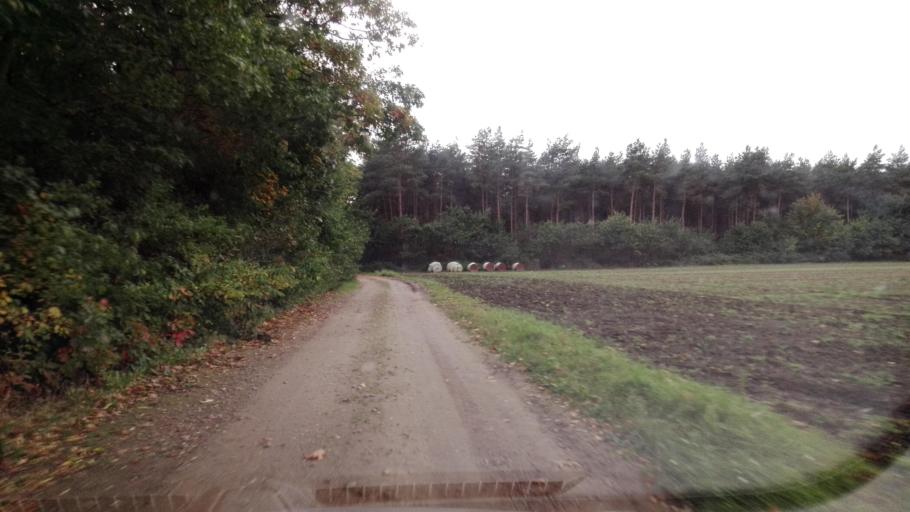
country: NL
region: Limburg
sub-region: Gemeente Venlo
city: Tegelen
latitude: 51.3975
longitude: 6.1178
